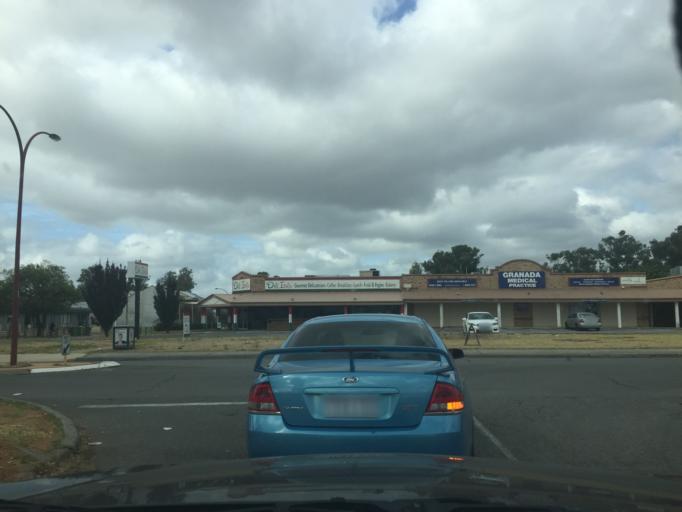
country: AU
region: Western Australia
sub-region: Gosnells
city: Maddington
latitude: -32.0525
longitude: 115.9799
